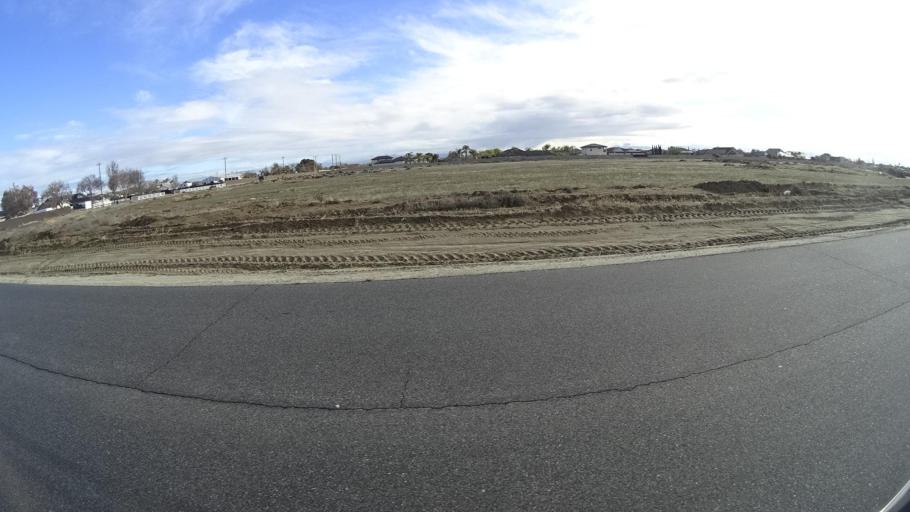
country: US
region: California
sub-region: Kern County
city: Rosedale
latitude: 35.3971
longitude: -119.1725
